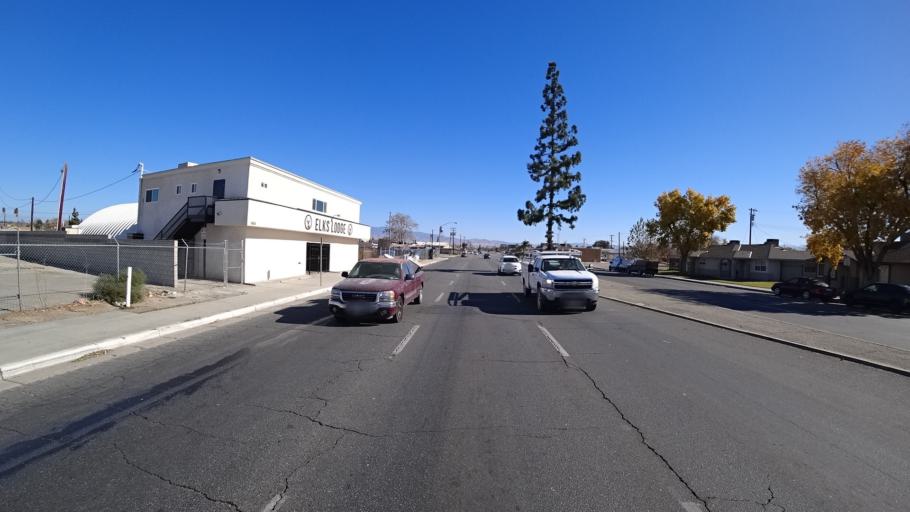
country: US
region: California
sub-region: Kern County
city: Bakersfield
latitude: 35.3686
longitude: -118.9836
